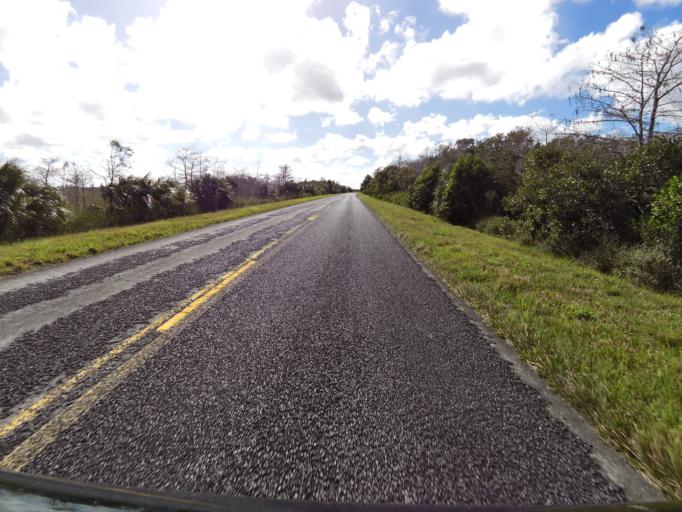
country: US
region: Florida
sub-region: Miami-Dade County
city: Florida City
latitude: 25.4031
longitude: -80.7903
